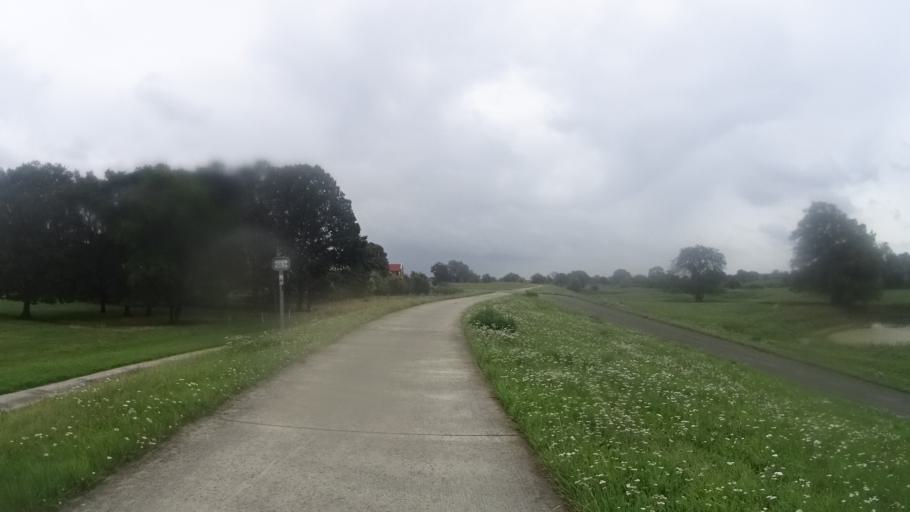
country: DE
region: Lower Saxony
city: Bleckede
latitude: 53.2986
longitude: 10.7524
